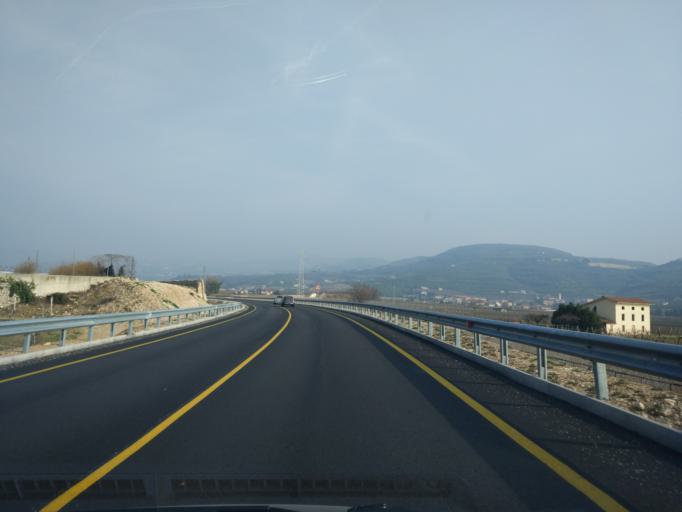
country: IT
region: Veneto
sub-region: Provincia di Verona
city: Poiano
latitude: 45.4837
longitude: 11.0229
